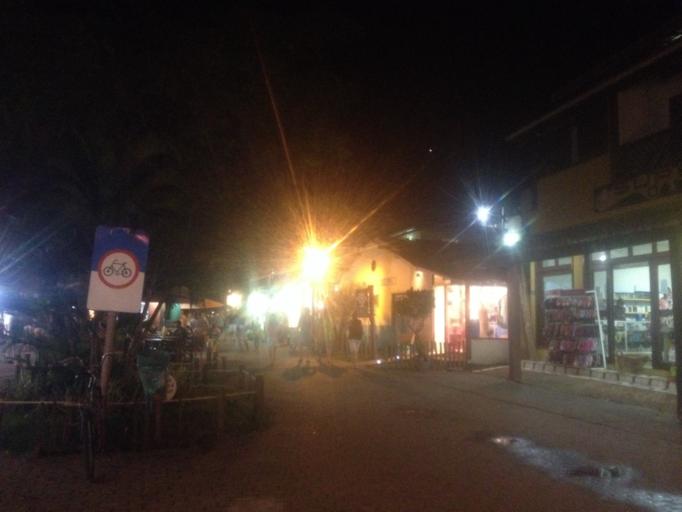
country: BR
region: Bahia
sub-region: Mata De Sao Joao
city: Mata de Sao Joao
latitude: -12.5778
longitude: -38.0054
